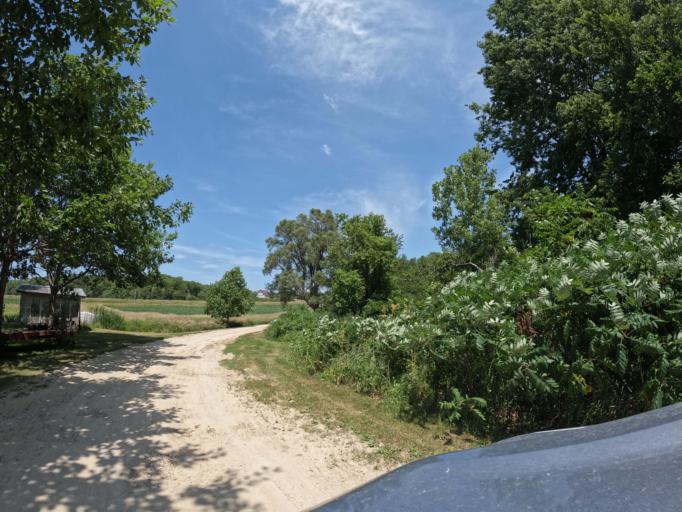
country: US
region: Iowa
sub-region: Henry County
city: Mount Pleasant
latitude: 40.9349
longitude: -91.6038
